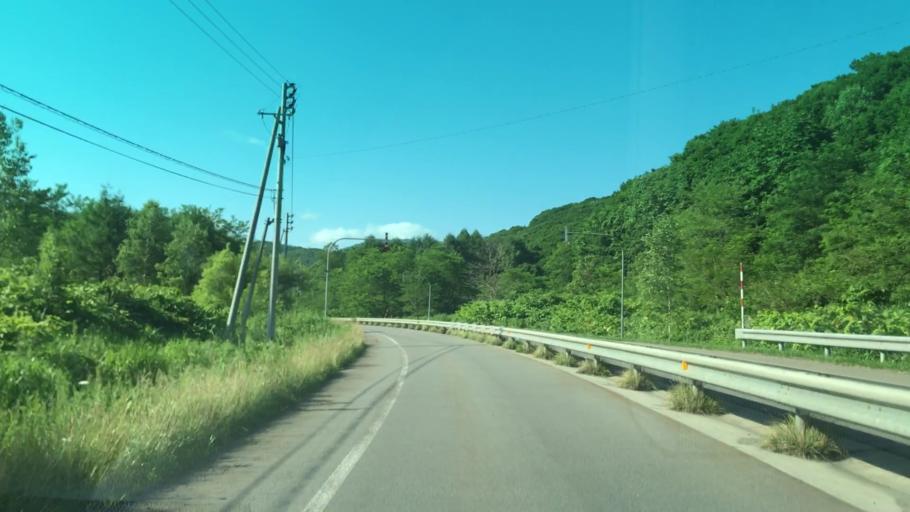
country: JP
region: Hokkaido
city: Iwanai
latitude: 43.0012
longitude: 140.6688
